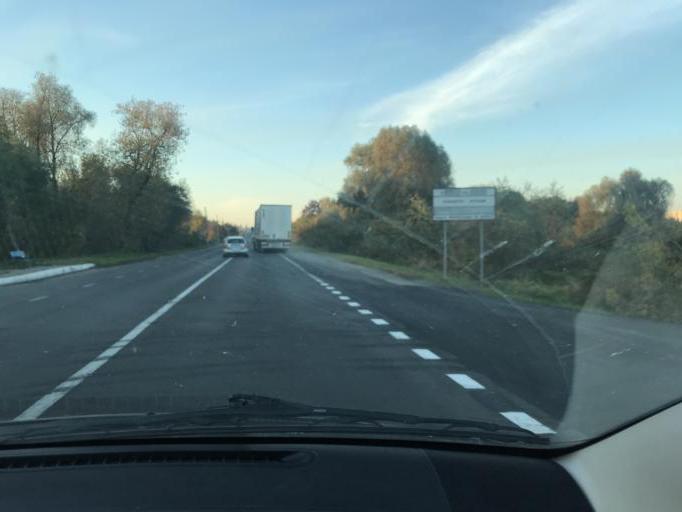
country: BY
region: Brest
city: Pinsk
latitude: 52.1045
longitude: 26.1110
